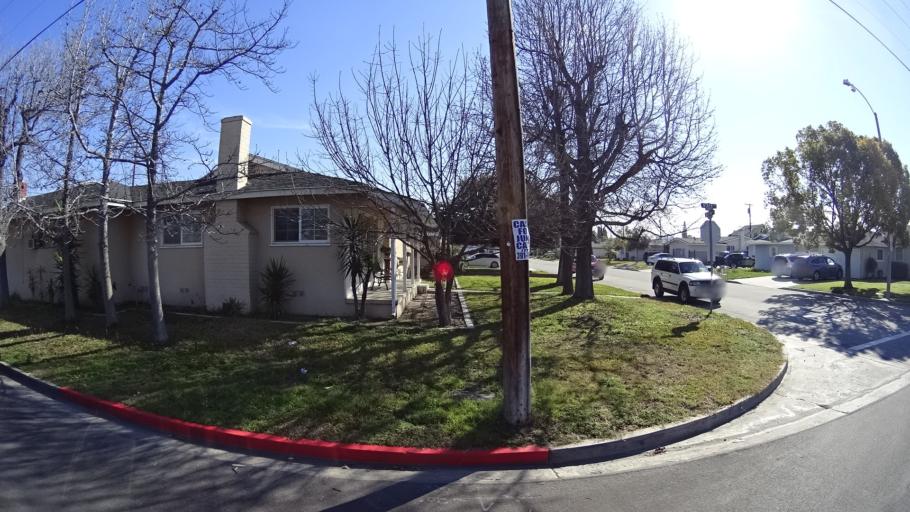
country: US
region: California
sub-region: Orange County
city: Garden Grove
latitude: 33.8051
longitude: -117.9327
